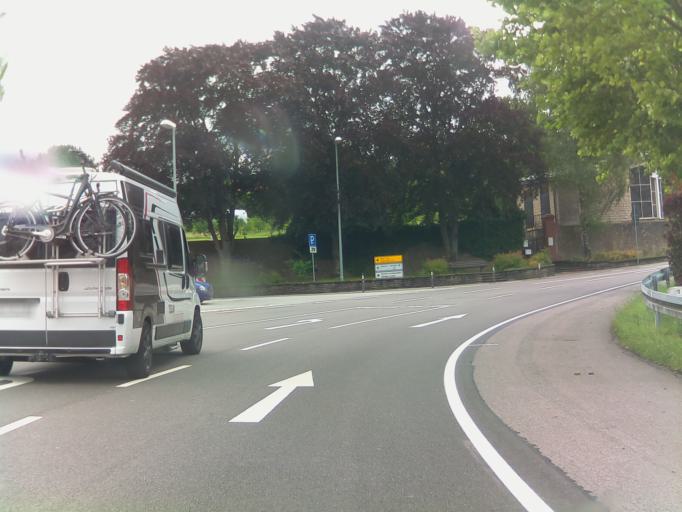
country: DE
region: Saarland
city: Perl
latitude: 49.4769
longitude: 6.3869
